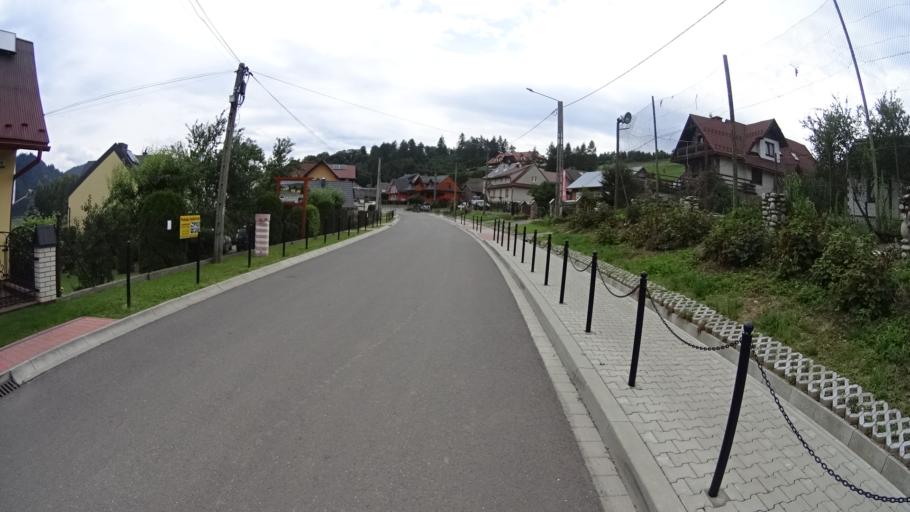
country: PL
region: Lesser Poland Voivodeship
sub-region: Powiat nowotarski
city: Niedzica
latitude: 49.4246
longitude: 20.3108
